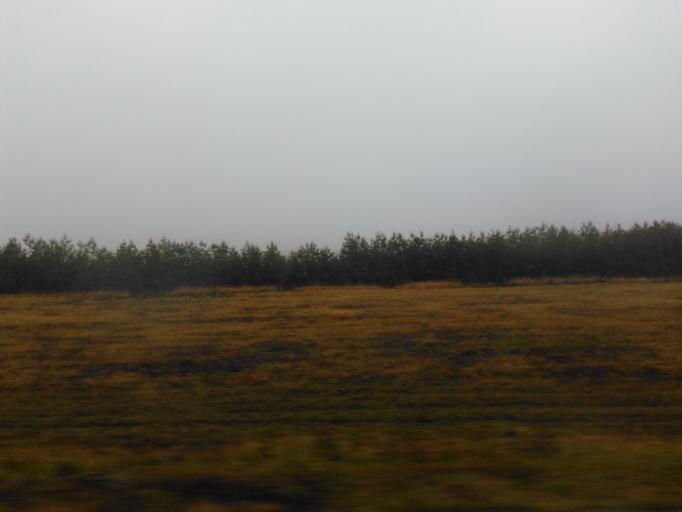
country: RU
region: Tatarstan
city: Sviyazhsk
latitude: 55.7369
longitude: 48.7825
